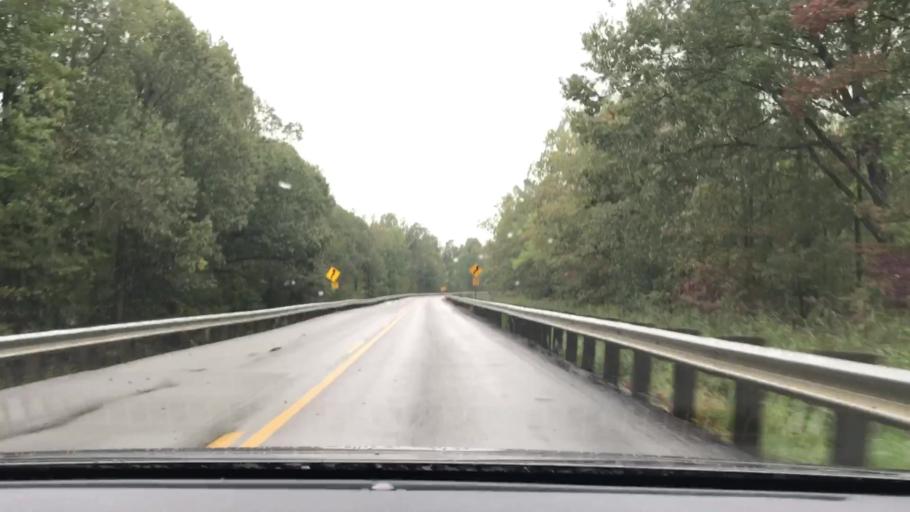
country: US
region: Kentucky
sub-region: McLean County
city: Calhoun
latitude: 37.3949
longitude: -87.2980
